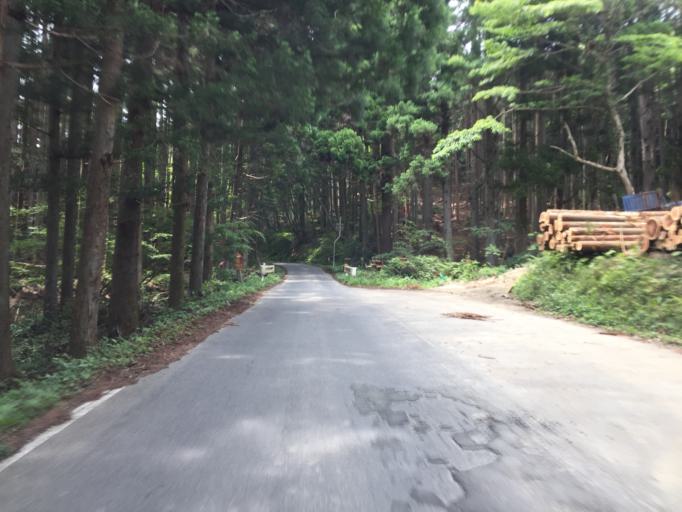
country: JP
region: Miyagi
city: Marumori
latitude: 37.8280
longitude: 140.8667
